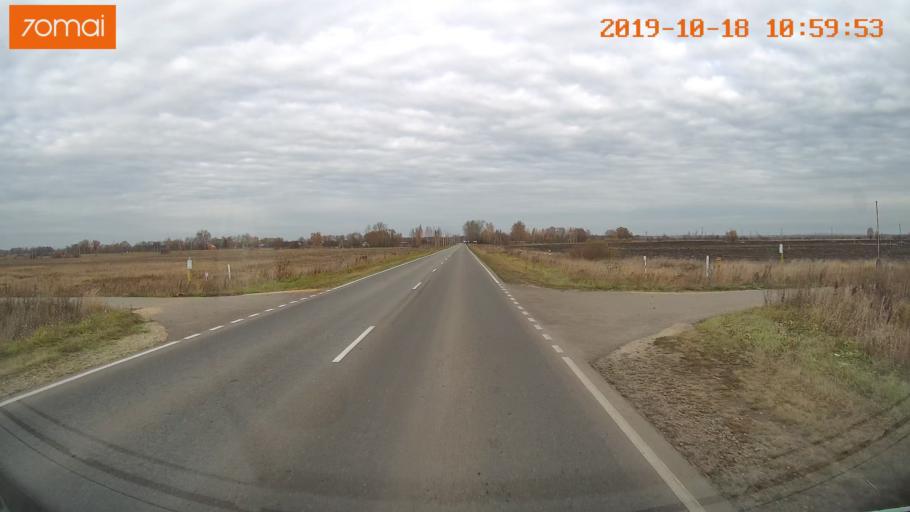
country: RU
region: Tula
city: Yepifan'
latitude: 53.8357
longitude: 38.5549
